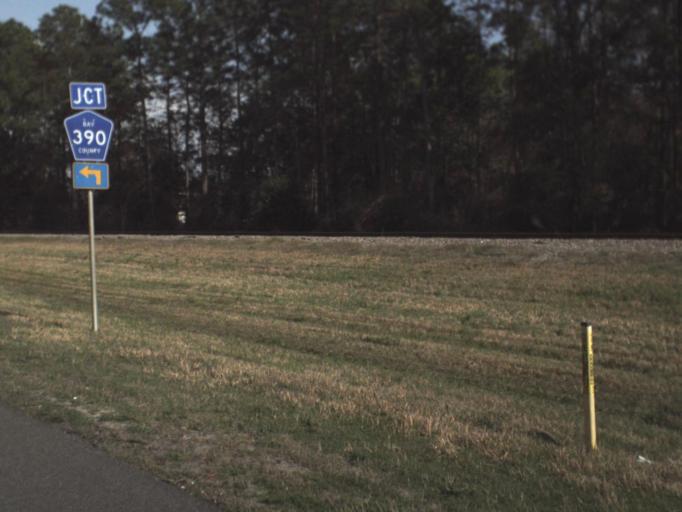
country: US
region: Florida
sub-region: Bay County
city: Hiland Park
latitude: 30.2326
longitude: -85.5799
